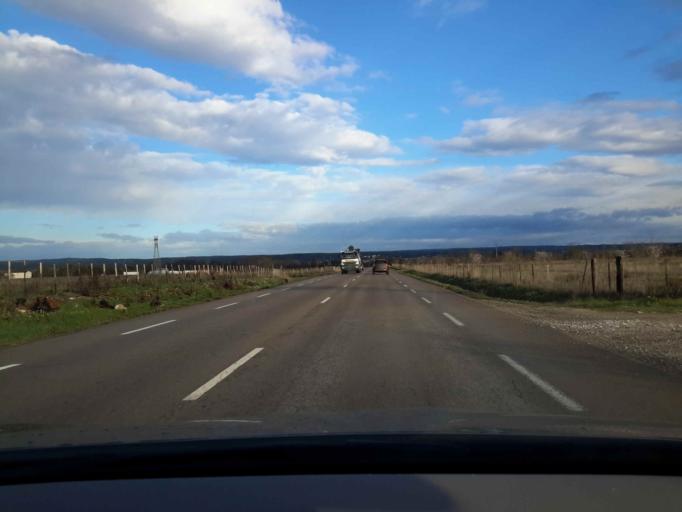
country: FR
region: Languedoc-Roussillon
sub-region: Departement du Gard
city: Aubord
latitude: 43.7645
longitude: 4.3317
